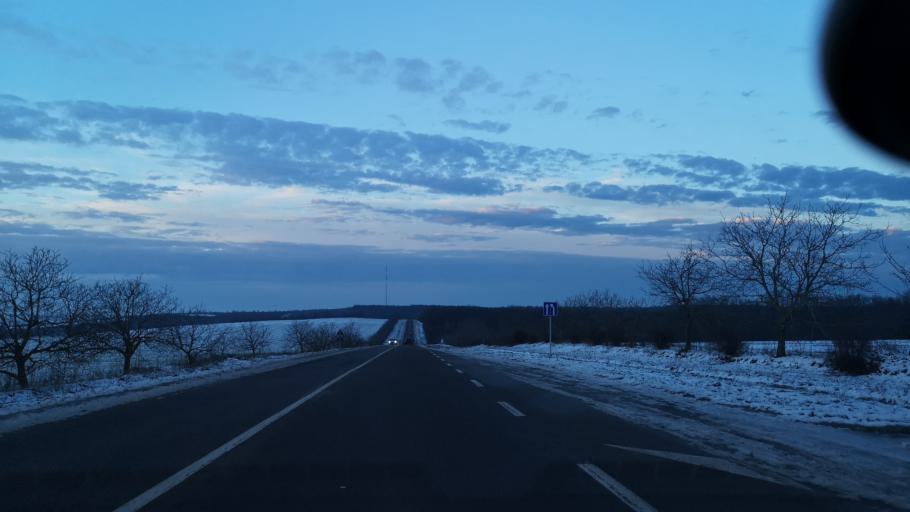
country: MD
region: Rezina
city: Saharna
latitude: 47.6350
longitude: 28.8366
